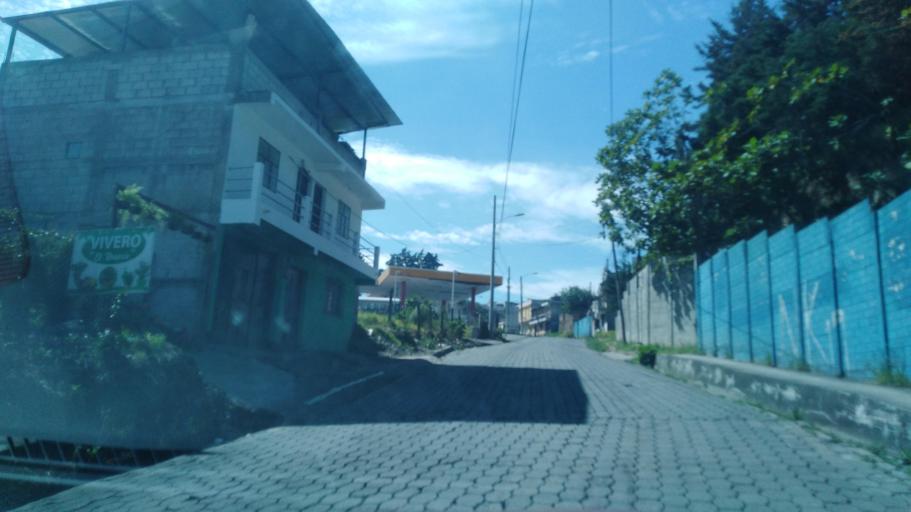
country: GT
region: Quetzaltenango
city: Quetzaltenango
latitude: 14.8484
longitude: -91.5140
